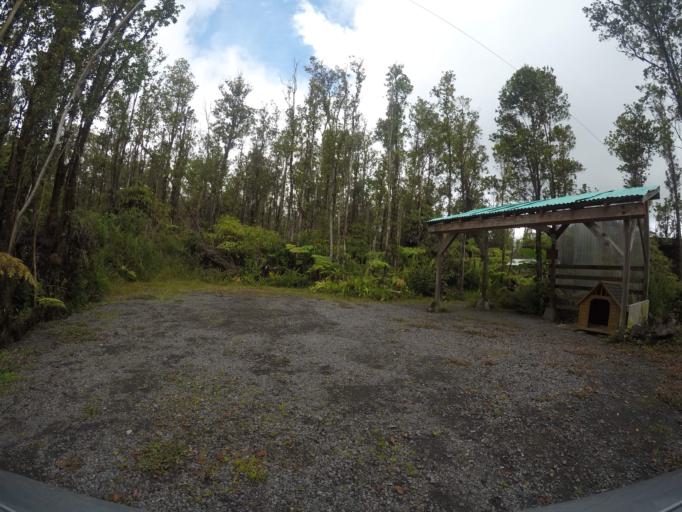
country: US
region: Hawaii
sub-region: Hawaii County
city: Fern Acres
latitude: 19.4658
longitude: -155.1215
